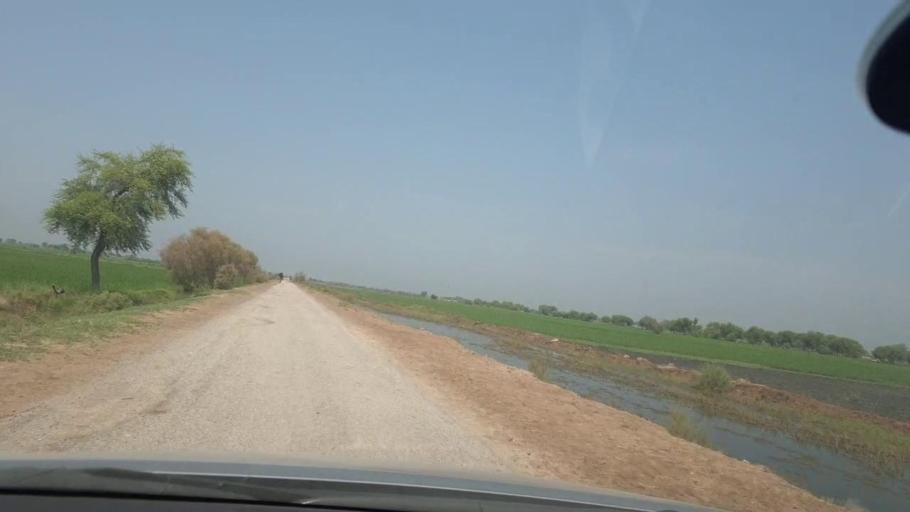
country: PK
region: Balochistan
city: Mehrabpur
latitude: 28.0673
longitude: 68.0578
